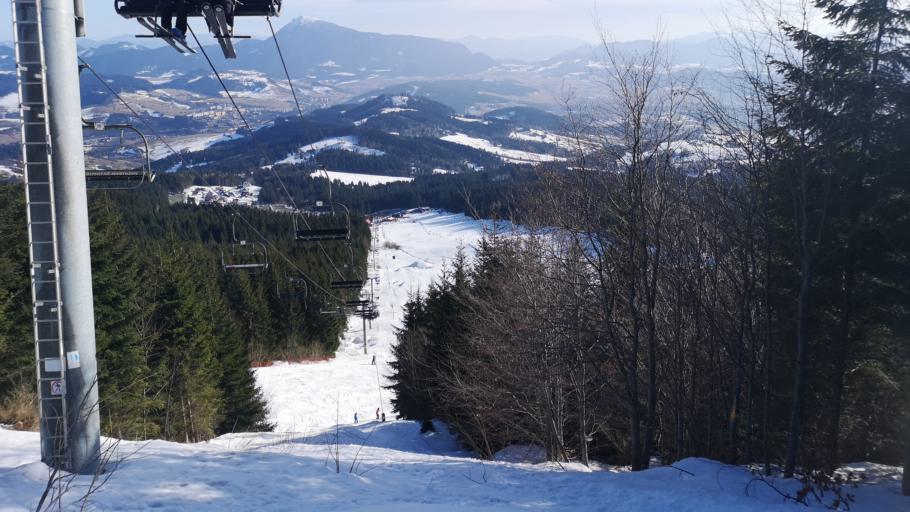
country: SK
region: Zilinsky
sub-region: Okres Dolny Kubin
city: Dolny Kubin
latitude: 49.2605
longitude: 19.2607
